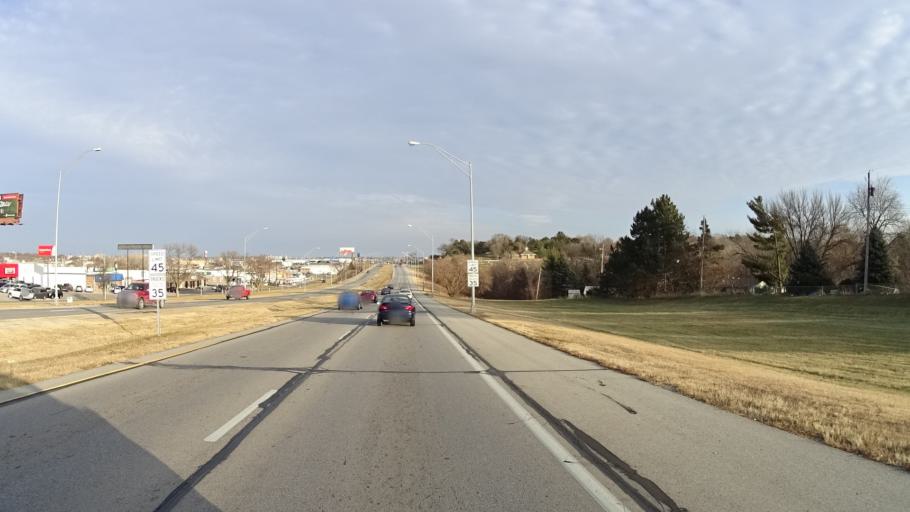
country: US
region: Nebraska
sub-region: Douglas County
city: Ralston
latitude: 41.2124
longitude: -96.0510
